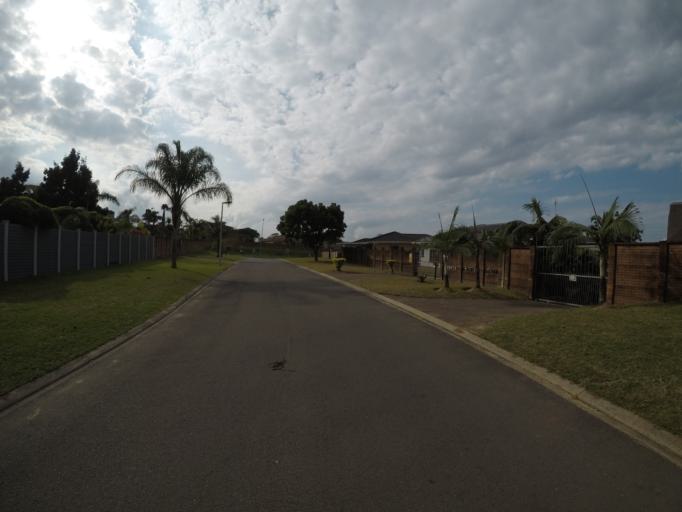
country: ZA
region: KwaZulu-Natal
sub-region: uThungulu District Municipality
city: Richards Bay
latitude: -28.7376
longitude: 32.0901
